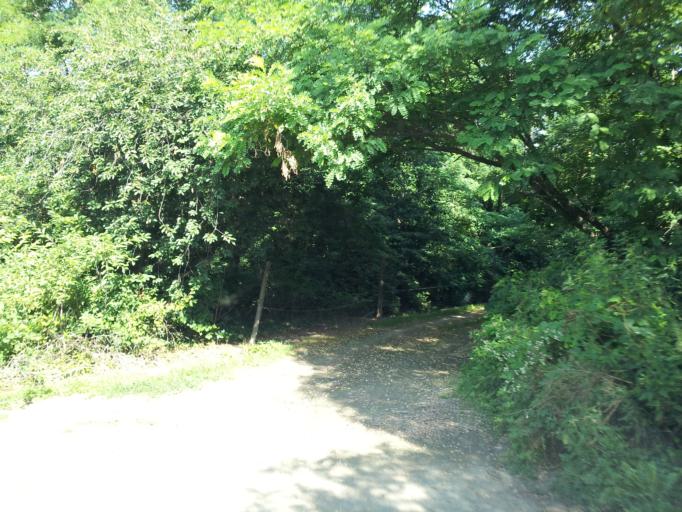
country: HU
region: Zala
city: Cserszegtomaj
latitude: 46.8484
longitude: 17.2188
